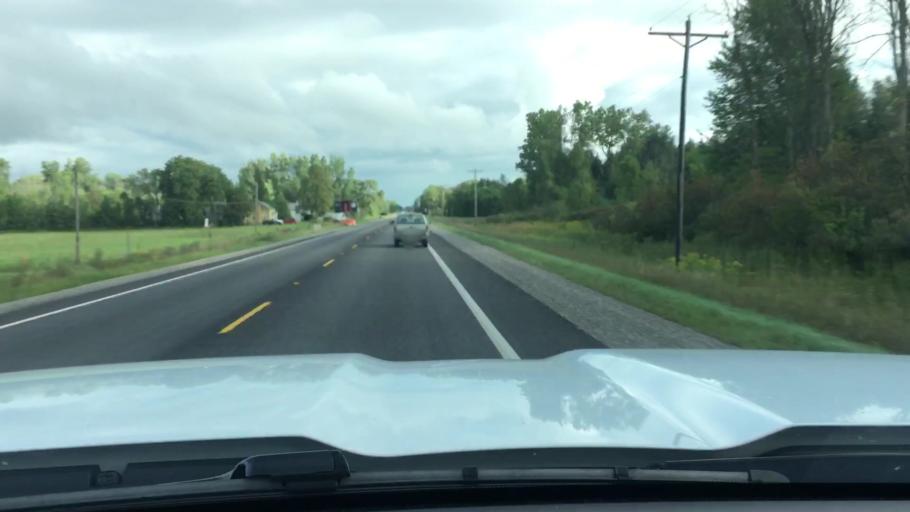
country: US
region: Michigan
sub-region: Tuscola County
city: Caro
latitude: 43.4363
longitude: -83.3850
